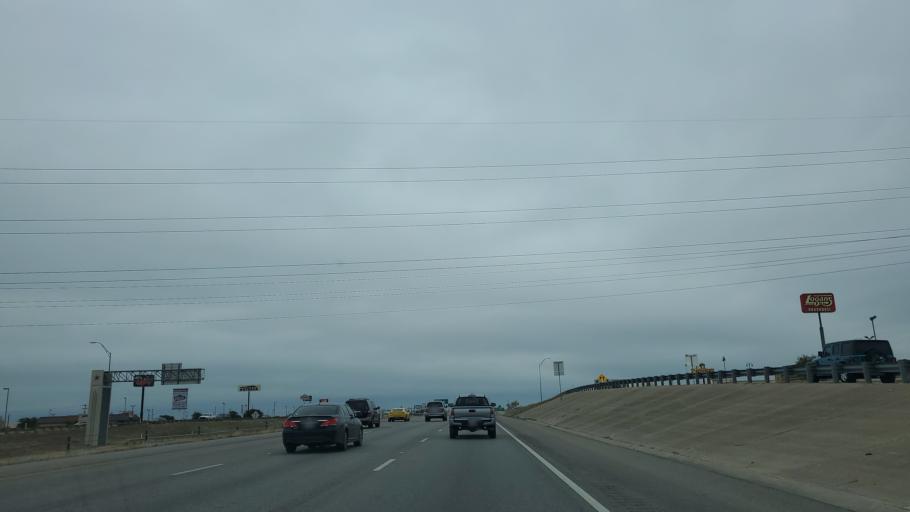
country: US
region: Texas
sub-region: Bell County
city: Killeen
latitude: 31.0878
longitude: -97.7139
